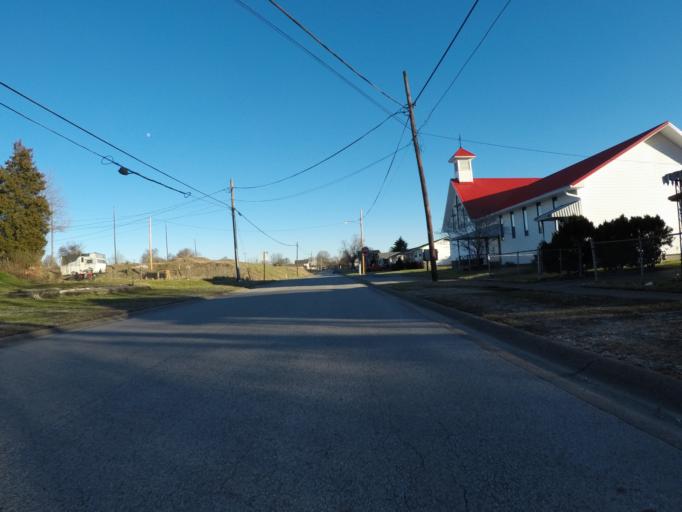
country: US
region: West Virginia
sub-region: Wayne County
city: Kenova
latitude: 38.3994
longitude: -82.5849
